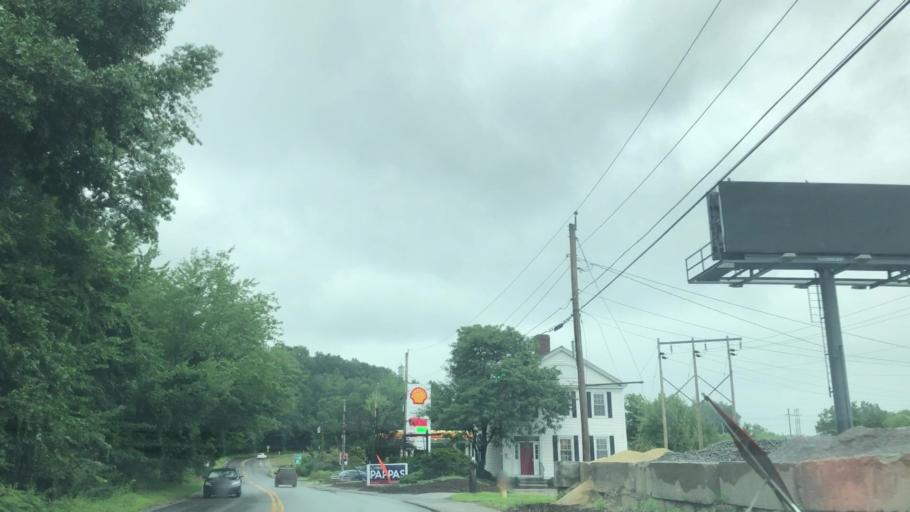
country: US
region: New Hampshire
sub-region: Hillsborough County
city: Manchester
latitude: 42.9992
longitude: -71.4755
